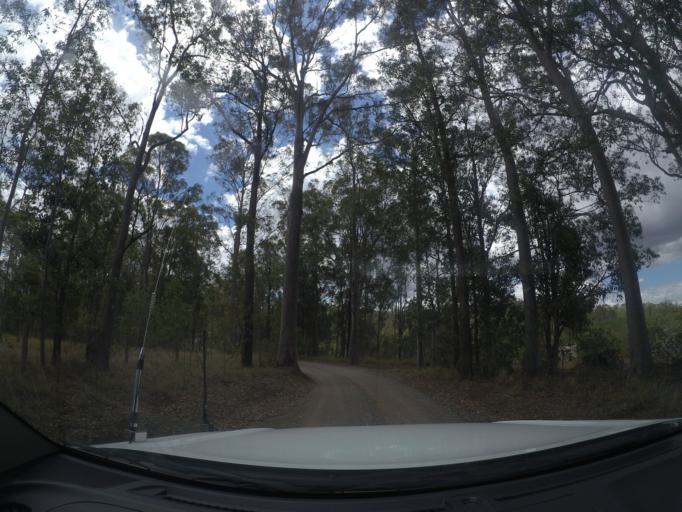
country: AU
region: Queensland
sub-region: Logan
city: Cedar Vale
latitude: -27.9098
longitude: 153.0314
